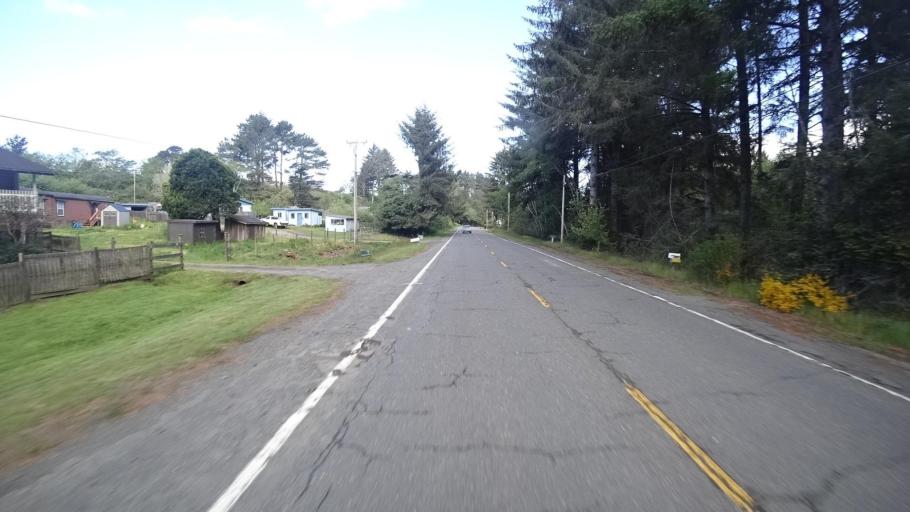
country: US
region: California
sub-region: Humboldt County
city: McKinleyville
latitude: 40.9869
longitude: -124.1078
